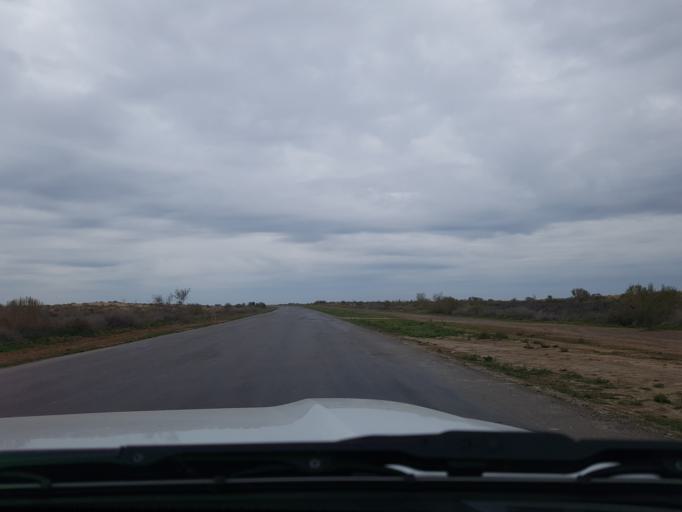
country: TM
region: Mary
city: Bayramaly
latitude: 37.6704
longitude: 62.3953
